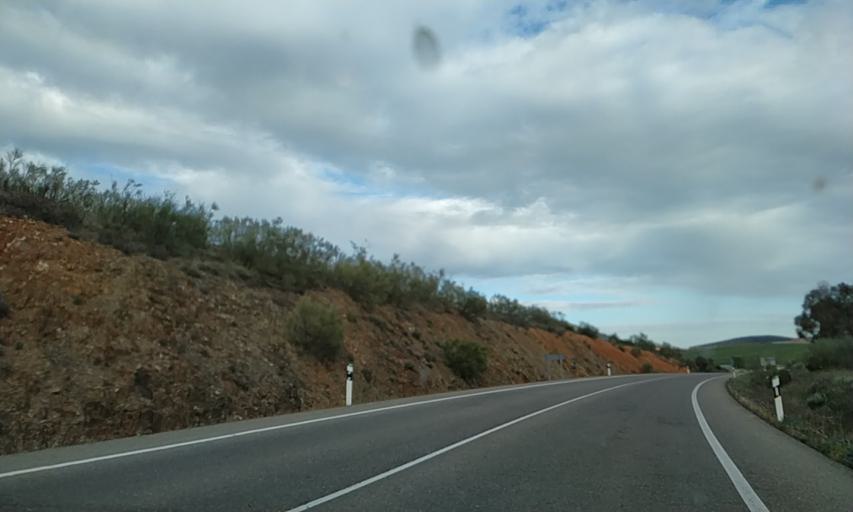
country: ES
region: Extremadura
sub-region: Provincia de Caceres
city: Pedroso de Acim
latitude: 39.8440
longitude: -6.4051
